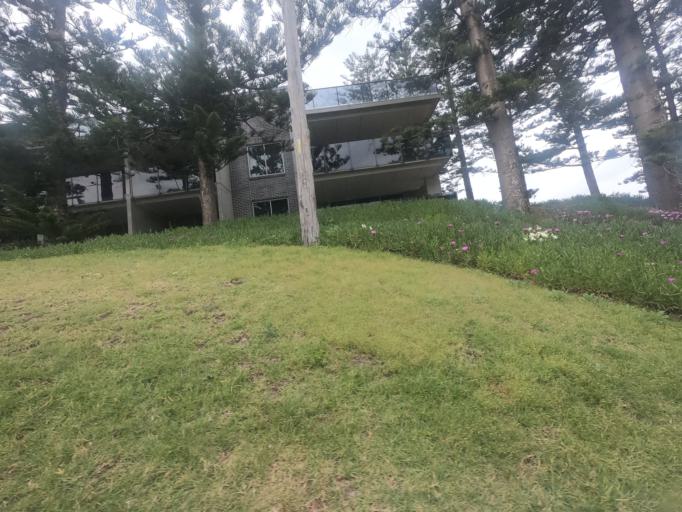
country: AU
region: New South Wales
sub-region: Wollongong
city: Bulli
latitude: -34.3017
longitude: 150.9398
